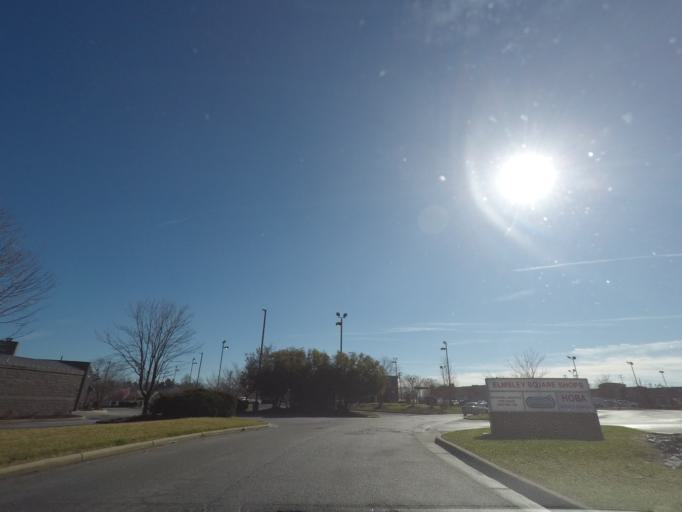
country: US
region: North Carolina
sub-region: Guilford County
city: Pleasant Garden
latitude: 36.0038
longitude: -79.7937
